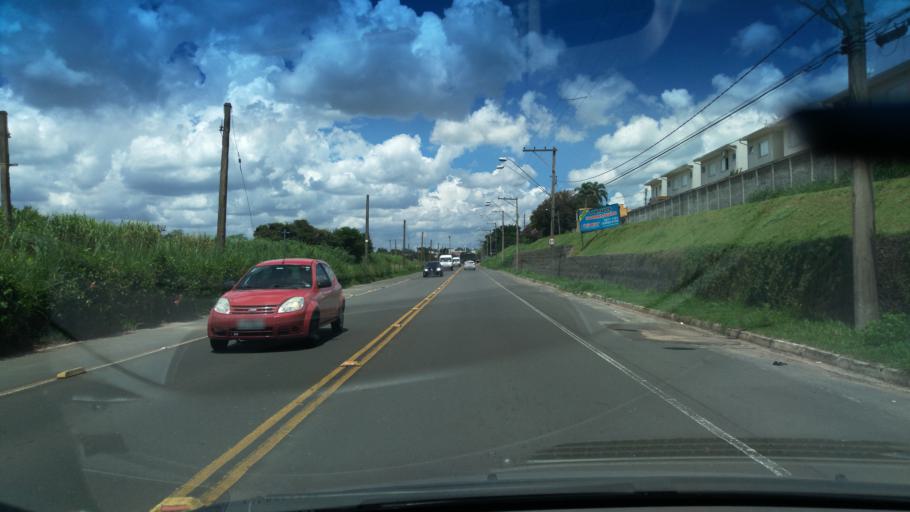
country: BR
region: Sao Paulo
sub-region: Valinhos
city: Valinhos
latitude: -22.9935
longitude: -46.9900
